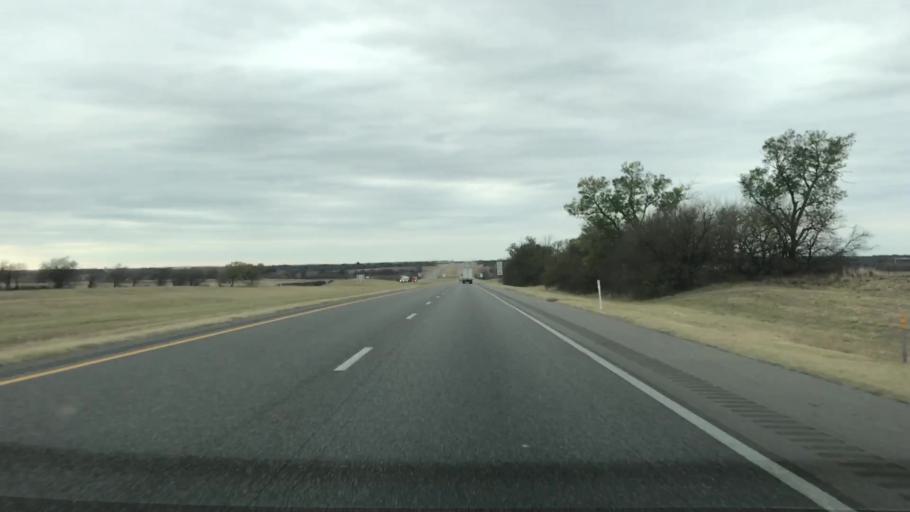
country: US
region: Oklahoma
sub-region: Beckham County
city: Erick
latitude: 35.2265
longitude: -99.8821
